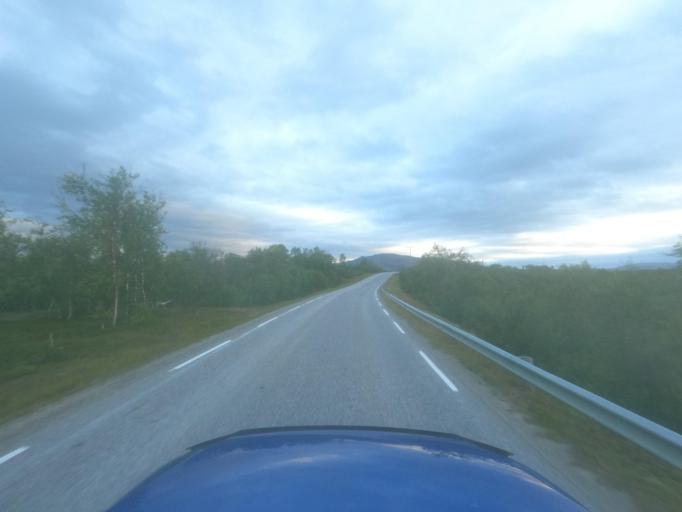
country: NO
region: Finnmark Fylke
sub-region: Porsanger
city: Lakselv
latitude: 70.1703
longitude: 24.9087
